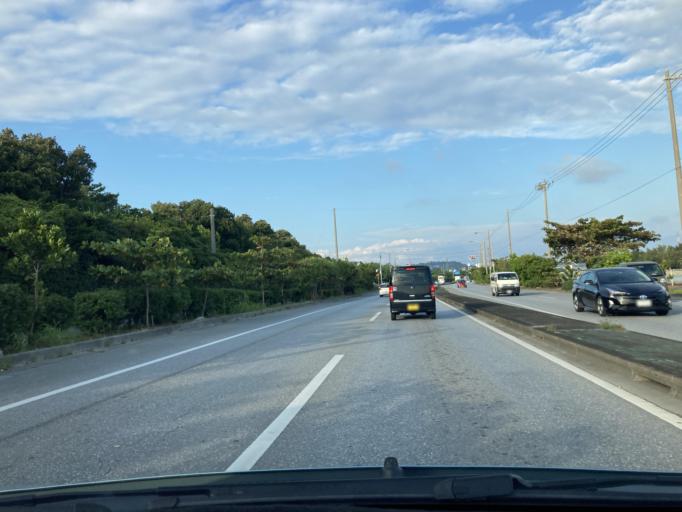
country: JP
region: Okinawa
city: Okinawa
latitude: 26.3276
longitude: 127.8352
